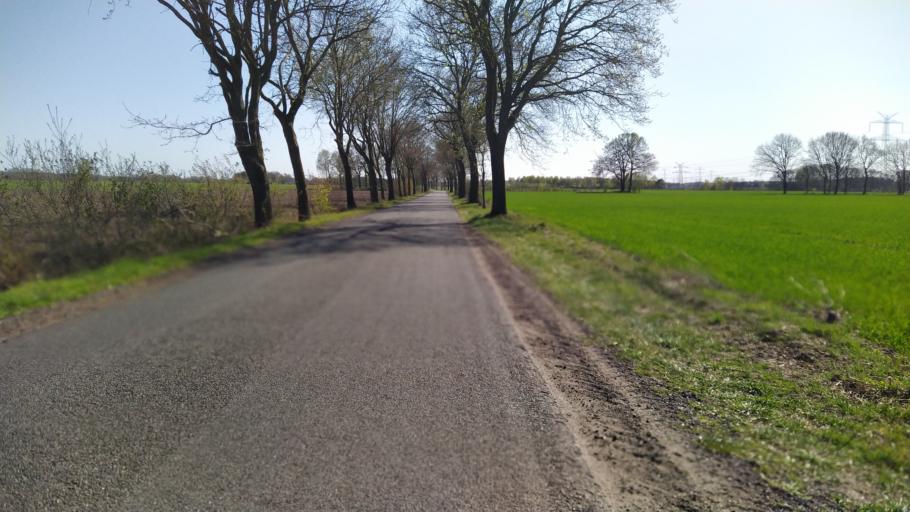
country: DE
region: Lower Saxony
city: Heeslingen
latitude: 53.3209
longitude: 9.3897
